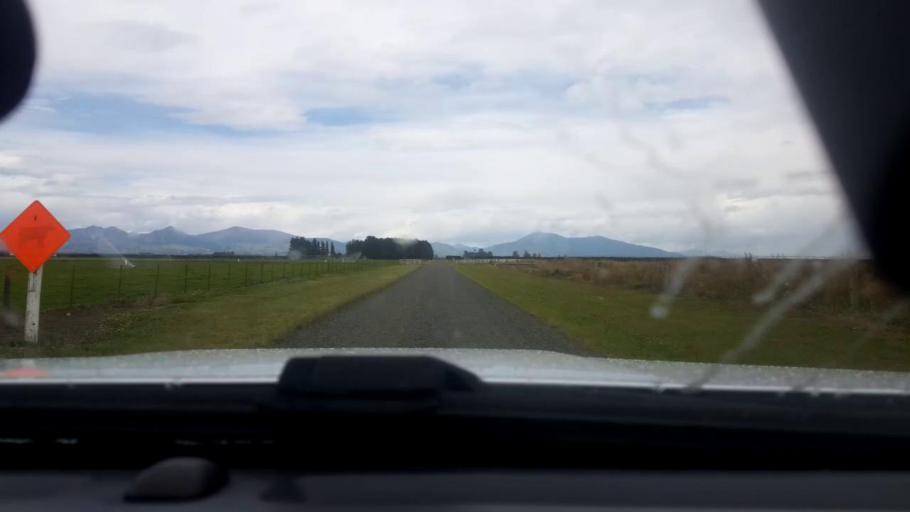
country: NZ
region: Canterbury
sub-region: Timaru District
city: Pleasant Point
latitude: -44.1148
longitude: 171.3553
